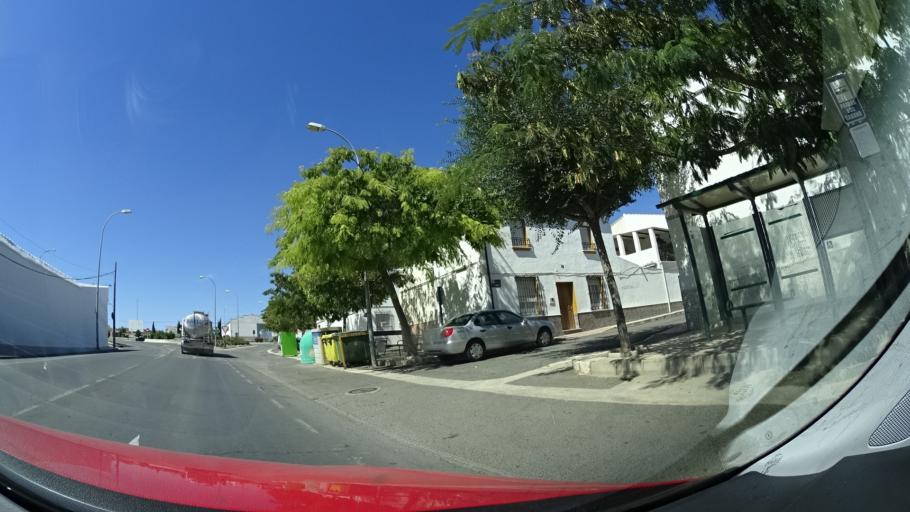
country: ES
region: Andalusia
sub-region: Provincia de Malaga
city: Campillos
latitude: 37.0528
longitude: -4.8627
